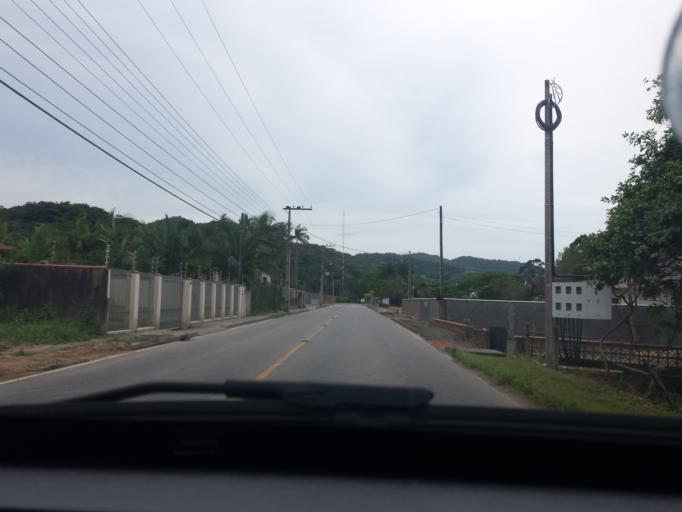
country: BR
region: Santa Catarina
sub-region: Gaspar
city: Gaspar
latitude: -26.8915
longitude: -49.0043
